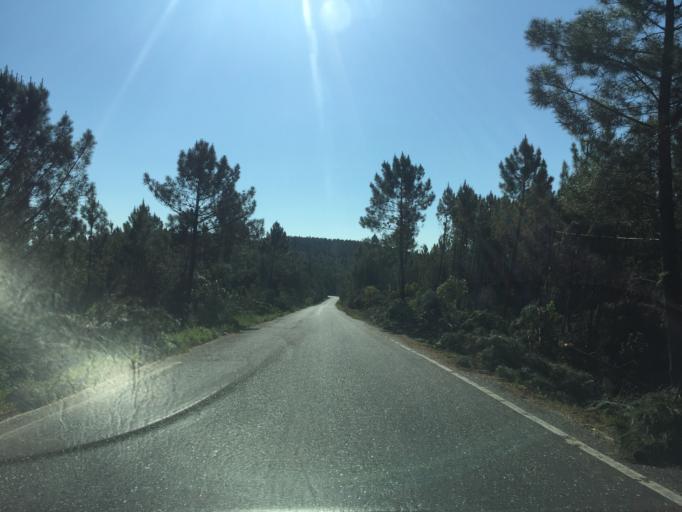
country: PT
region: Coimbra
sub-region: Pampilhosa da Serra
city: Pampilhosa da Serra
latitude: 40.0513
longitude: -7.8373
